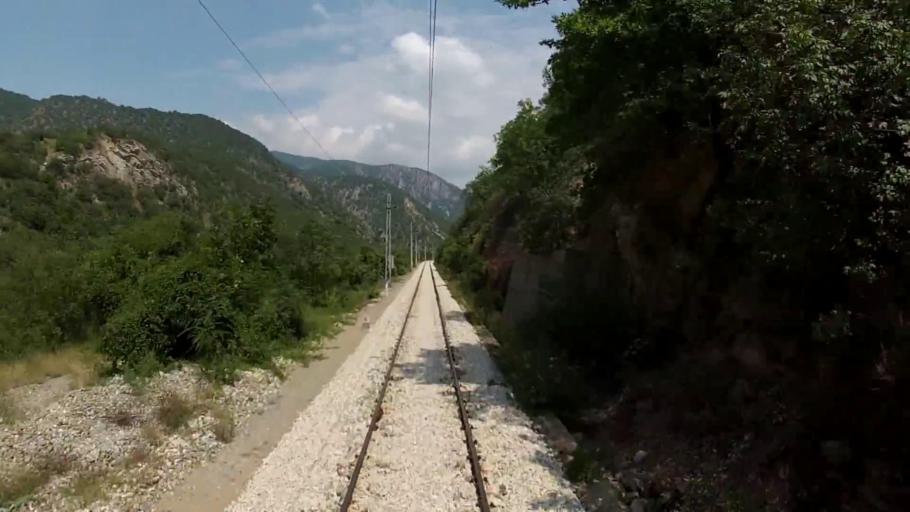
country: BG
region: Blagoevgrad
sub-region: Obshtina Kresna
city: Kresna
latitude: 41.7561
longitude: 23.1532
